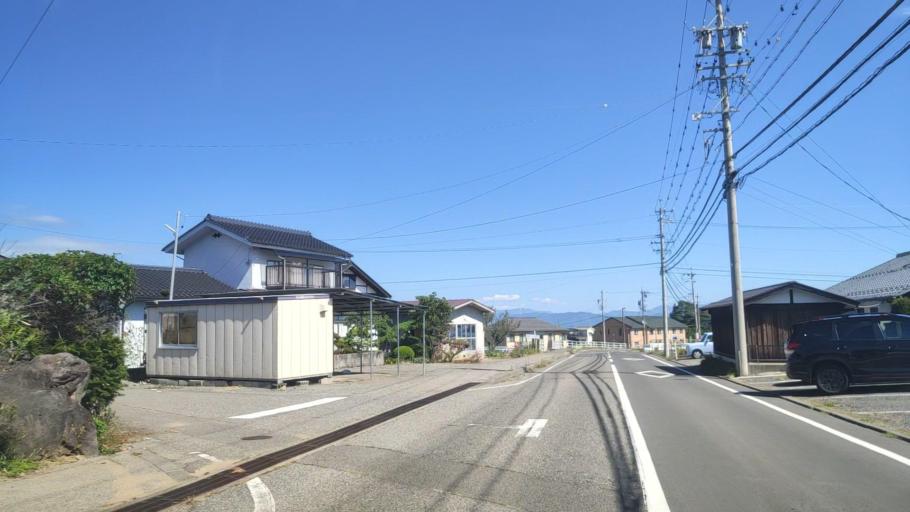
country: JP
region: Nagano
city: Toyoshina
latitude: 36.1987
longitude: 137.8600
